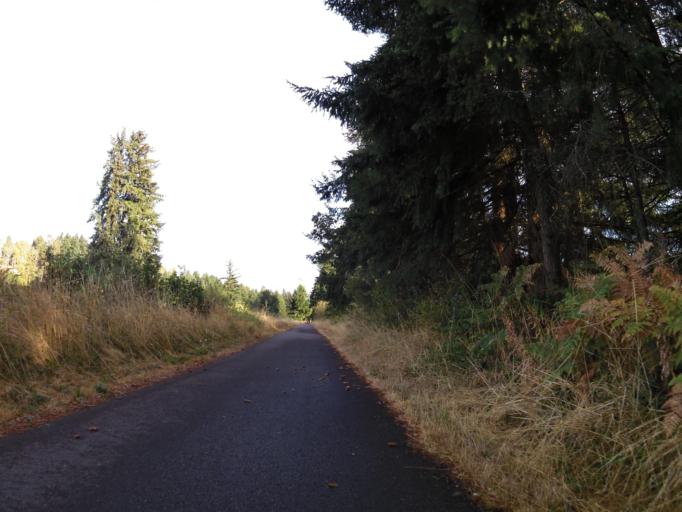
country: US
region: Washington
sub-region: Thurston County
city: Rainier
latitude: 46.8850
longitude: -122.7427
